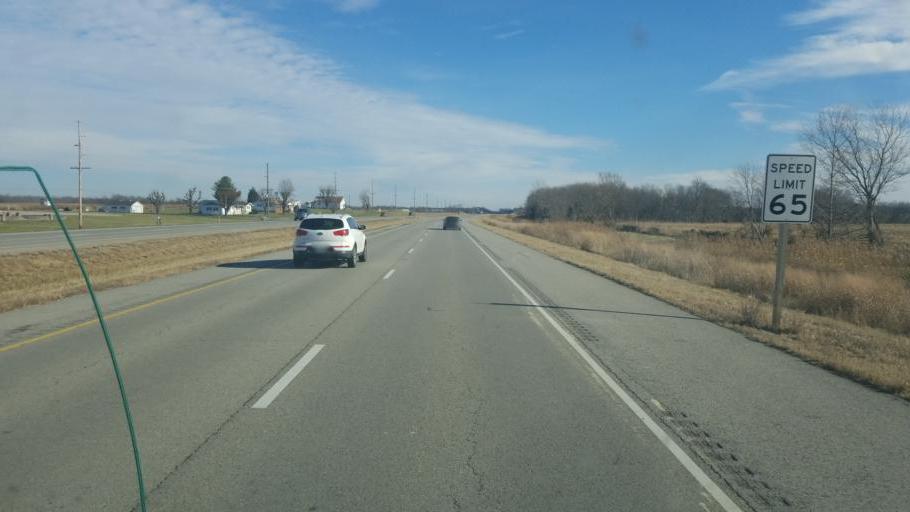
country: US
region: Illinois
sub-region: Williamson County
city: Marion
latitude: 37.7292
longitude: -88.8508
